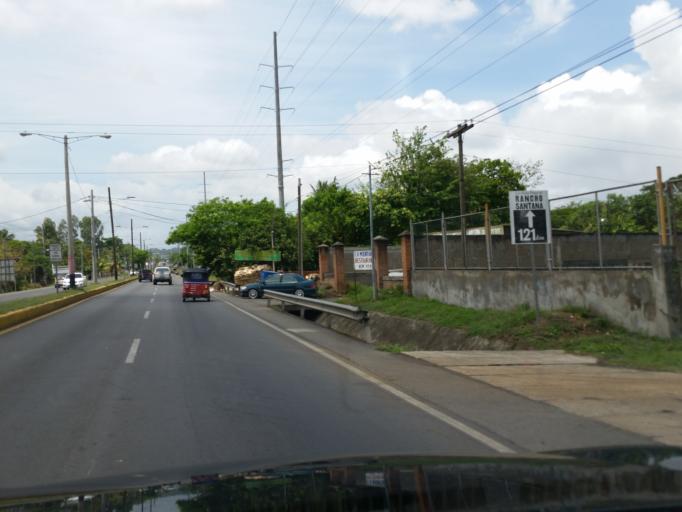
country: NI
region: Masaya
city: Ticuantepe
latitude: 12.0538
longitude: -86.2013
